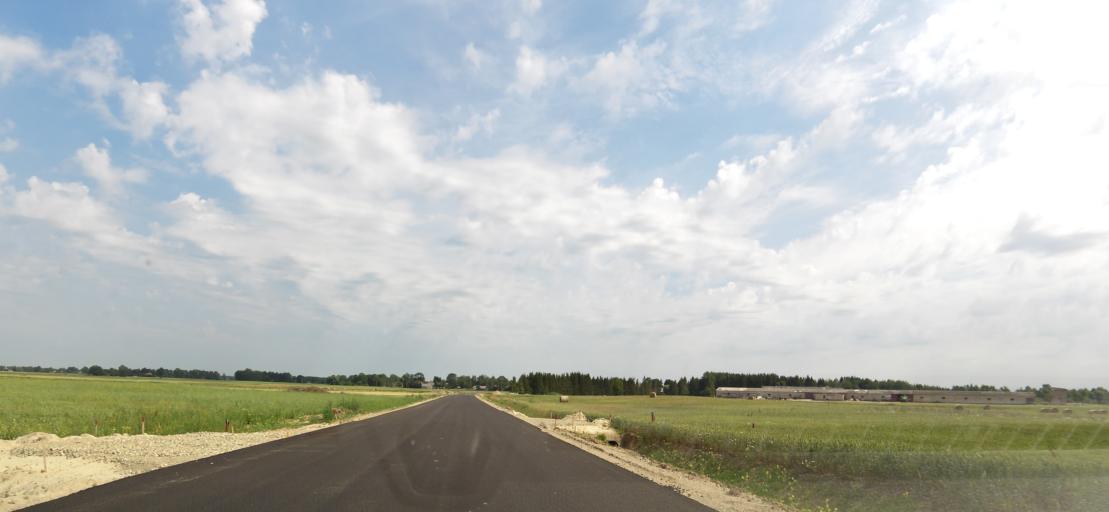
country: LT
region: Panevezys
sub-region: Birzai
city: Birzai
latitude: 56.2987
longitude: 24.6128
